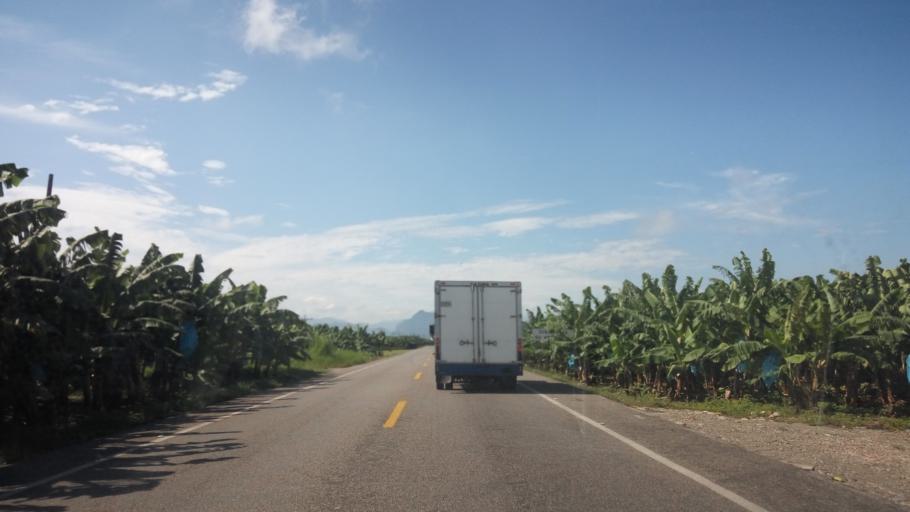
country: MX
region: Tabasco
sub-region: Teapa
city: Eureka y Belen
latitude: 17.6489
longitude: -92.9647
